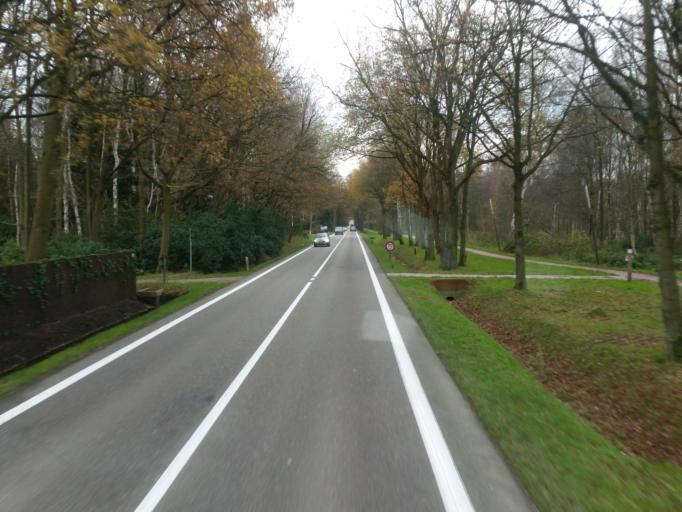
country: BE
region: Flanders
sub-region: Provincie Antwerpen
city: Brasschaat
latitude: 51.3394
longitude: 4.5164
